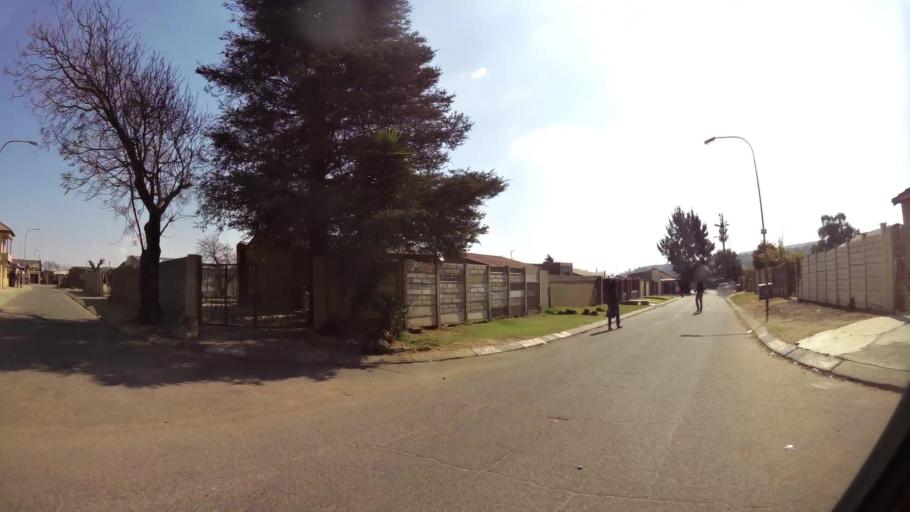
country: ZA
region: Gauteng
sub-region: City of Johannesburg Metropolitan Municipality
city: Johannesburg
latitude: -26.2402
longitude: 27.9568
